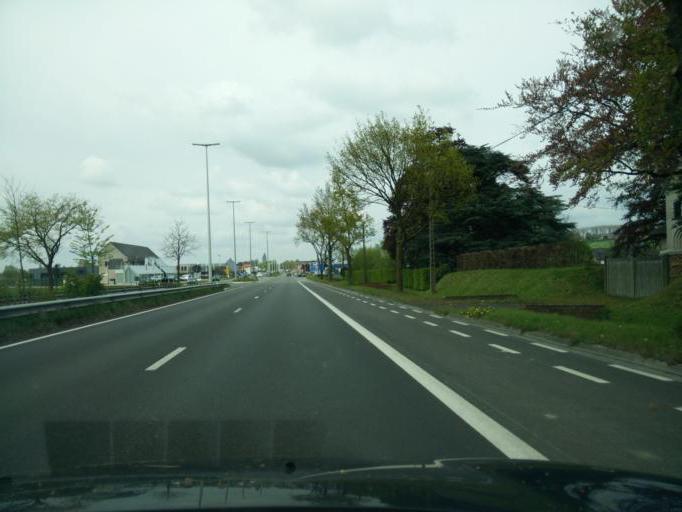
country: BE
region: Flanders
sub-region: Provincie Oost-Vlaanderen
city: Oudenaarde
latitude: 50.8216
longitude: 3.6039
